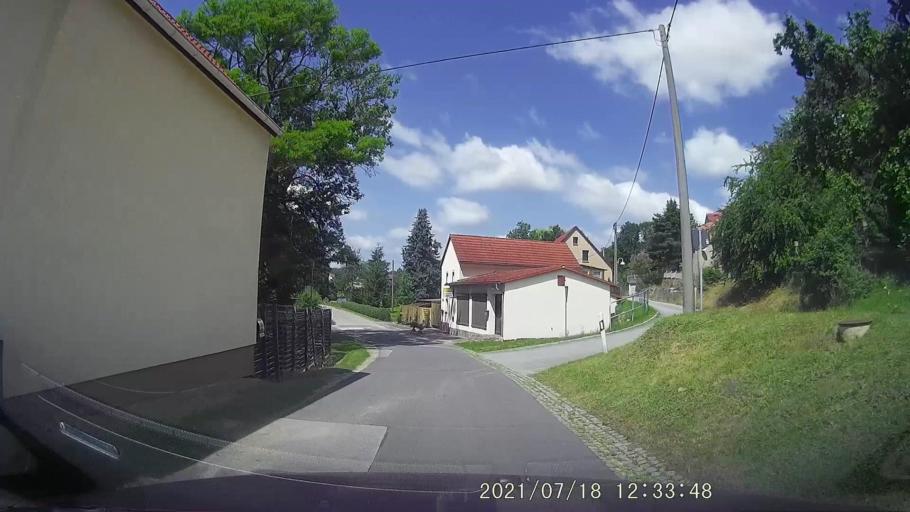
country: DE
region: Saxony
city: Konigshain
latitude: 51.1804
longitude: 14.8855
